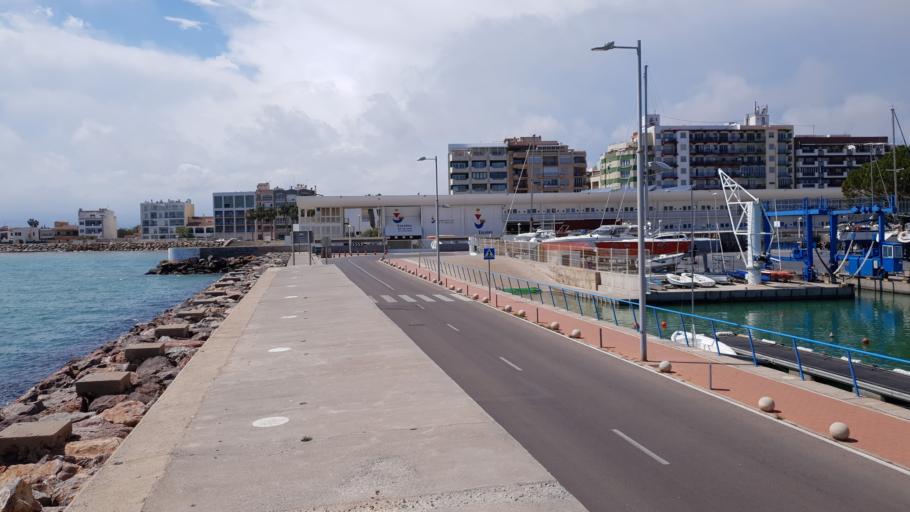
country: ES
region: Valencia
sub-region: Provincia de Castello
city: Burriana
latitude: 39.8613
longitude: -0.0748
